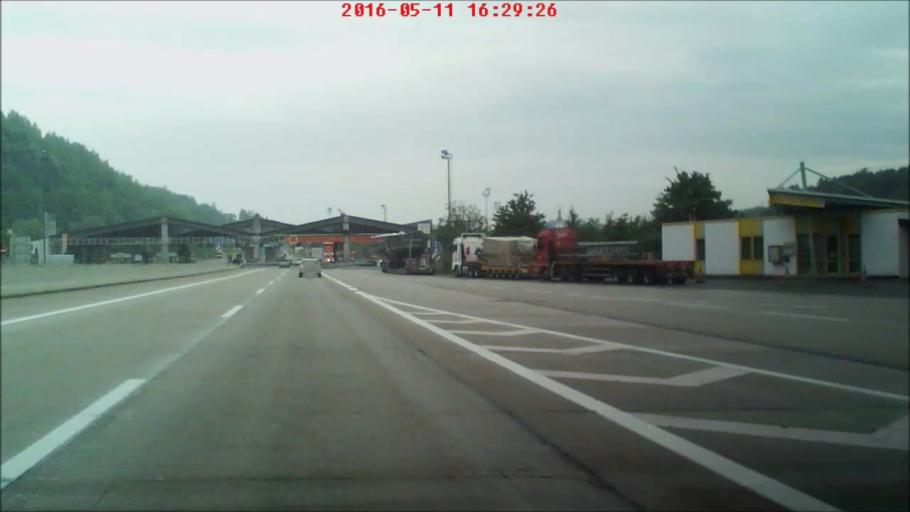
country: SI
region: Sentilj
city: Sentilj v Slov. Goricah
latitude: 46.6925
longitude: 15.6436
